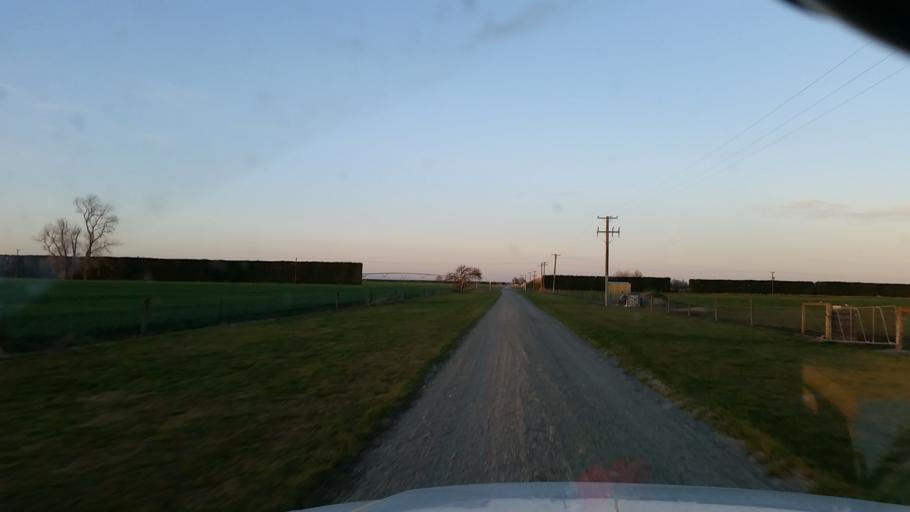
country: NZ
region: Canterbury
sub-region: Ashburton District
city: Tinwald
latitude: -43.9543
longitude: 171.5550
